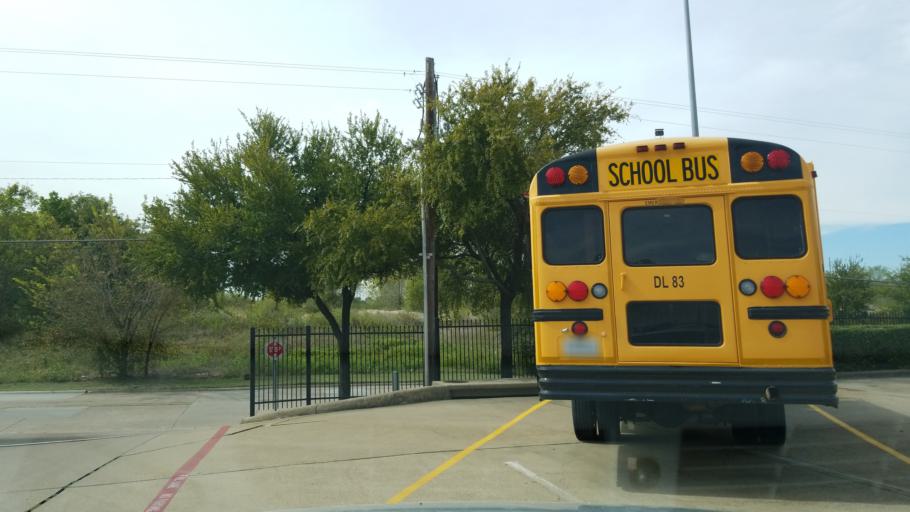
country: US
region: Texas
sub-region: Dallas County
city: Dallas
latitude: 32.7859
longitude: -96.7227
